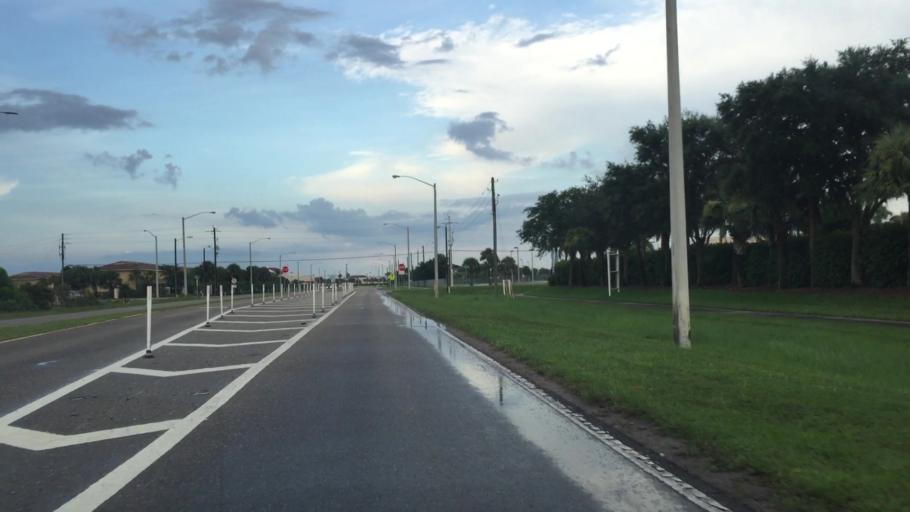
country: US
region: Florida
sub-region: Lee County
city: Fort Myers
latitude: 26.6028
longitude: -81.8197
